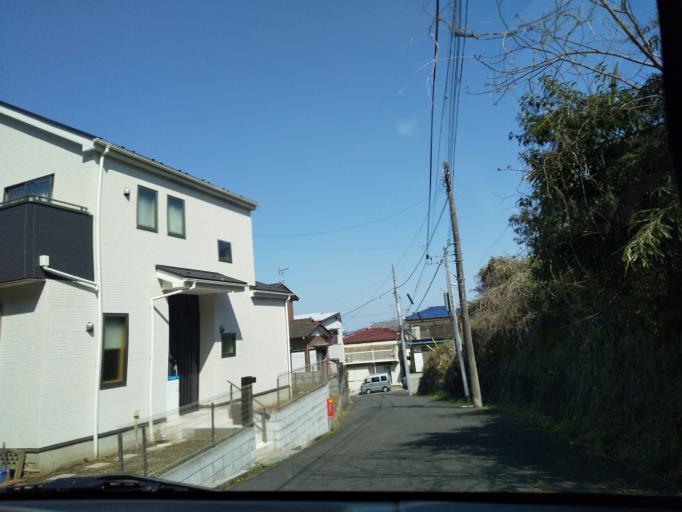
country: JP
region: Tokyo
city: Hino
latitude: 35.6409
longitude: 139.3785
